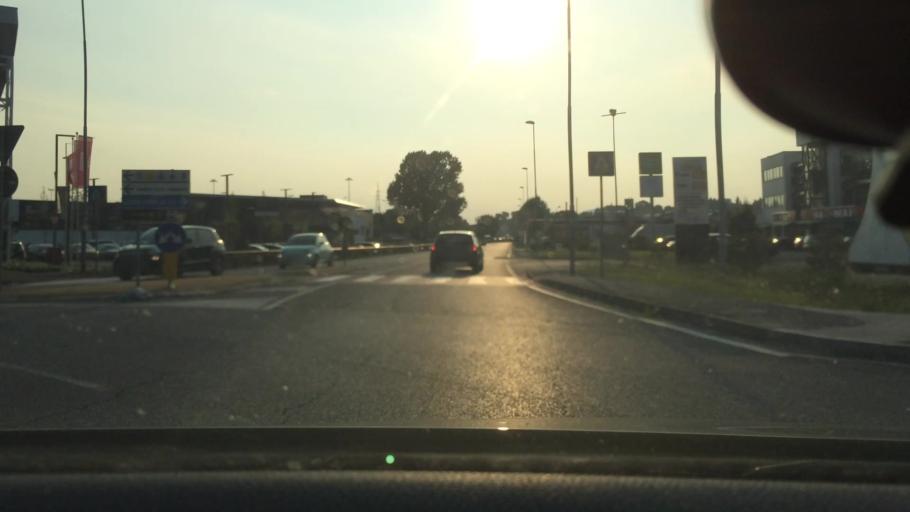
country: IT
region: Lombardy
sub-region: Provincia di Bergamo
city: Curno
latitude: 45.6916
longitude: 9.6244
